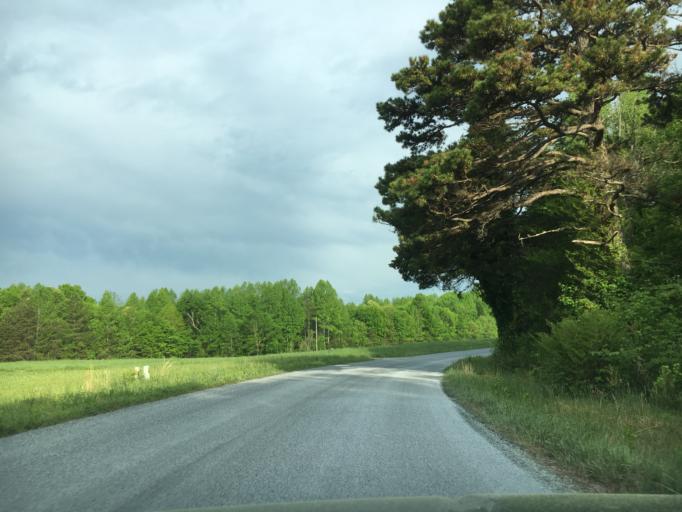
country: US
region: Virginia
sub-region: Campbell County
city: Brookneal
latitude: 36.9573
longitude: -78.9767
